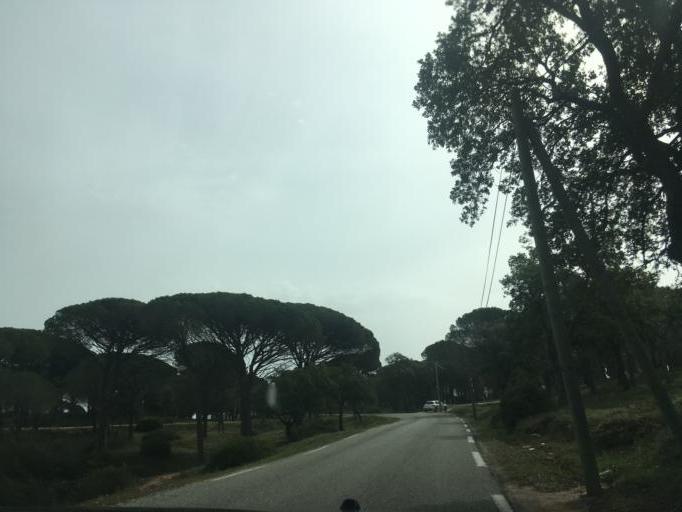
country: FR
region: Provence-Alpes-Cote d'Azur
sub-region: Departement du Var
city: Le Muy
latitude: 43.5072
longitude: 6.5985
